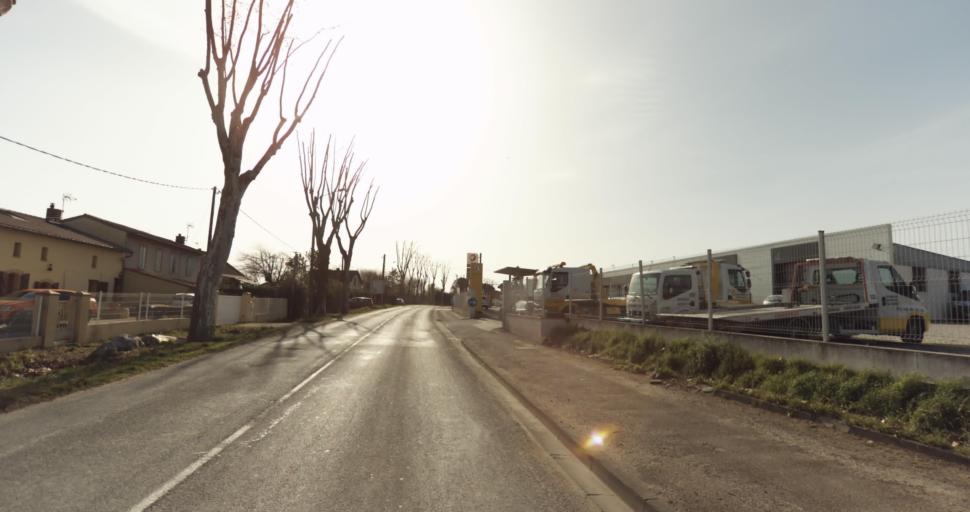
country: FR
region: Midi-Pyrenees
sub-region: Departement du Tarn
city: Saint-Sulpice-la-Pointe
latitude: 43.7672
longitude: 1.6916
